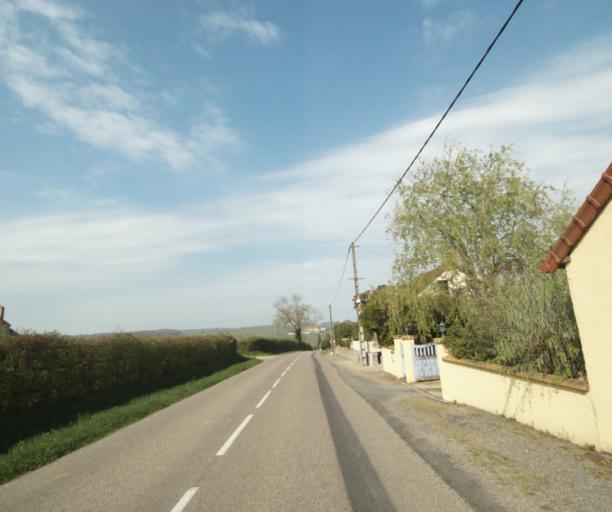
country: FR
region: Bourgogne
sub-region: Departement de Saone-et-Loire
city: Palinges
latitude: 46.5059
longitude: 4.1910
